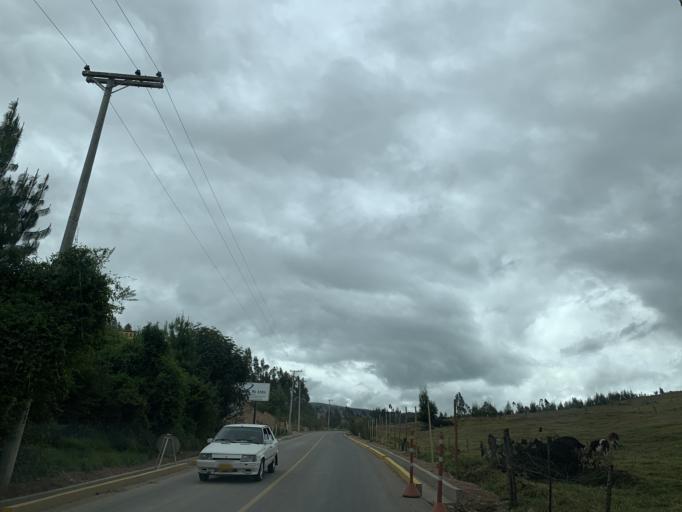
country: CO
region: Boyaca
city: Tunja
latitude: 5.5303
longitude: -73.3351
